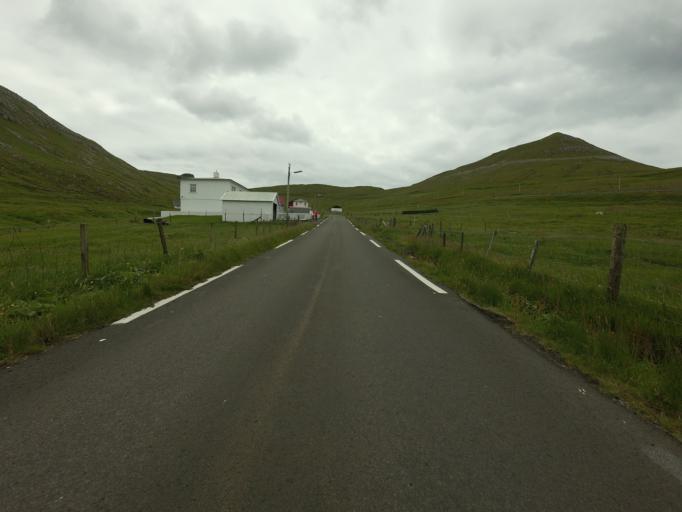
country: FO
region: Suduroy
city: Vagur
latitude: 61.4427
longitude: -6.7709
